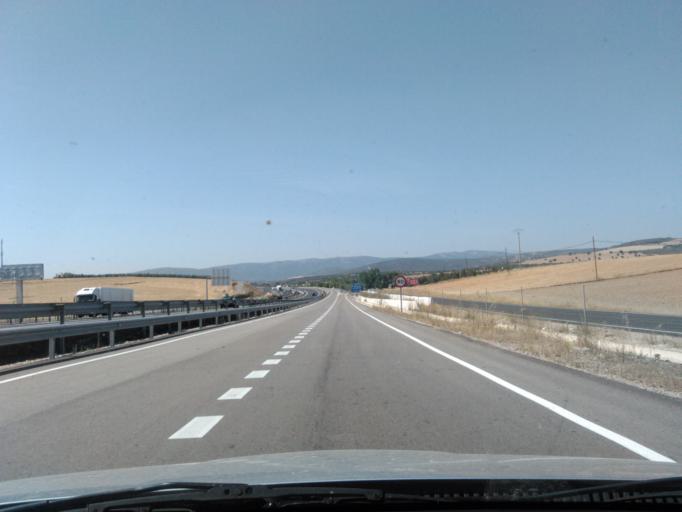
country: ES
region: Castille-La Mancha
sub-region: Provincia de Ciudad Real
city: Viso del Marques
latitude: 38.5026
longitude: -3.5010
